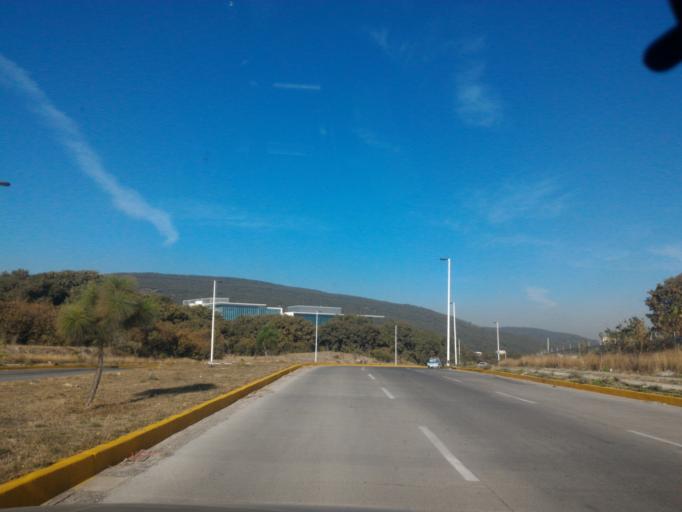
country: MX
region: Jalisco
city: Guadalajara
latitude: 20.6667
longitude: -103.4588
